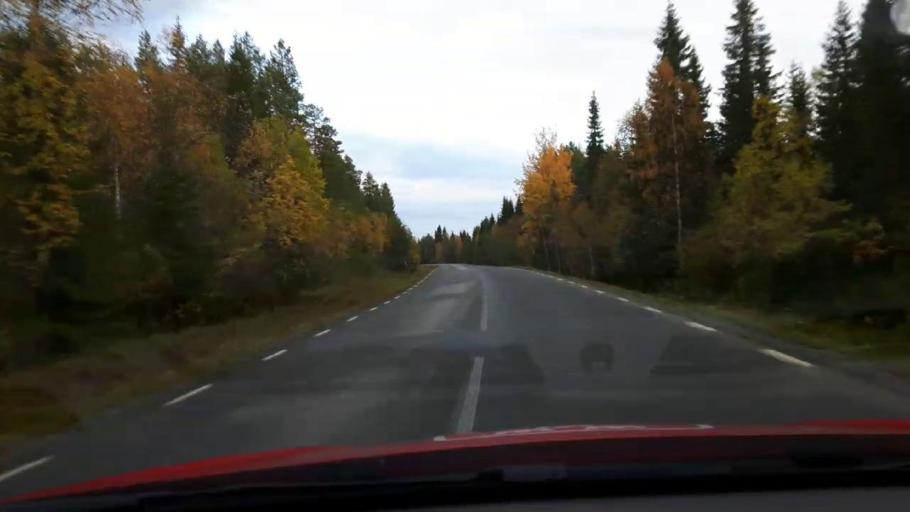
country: SE
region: Jaemtland
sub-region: OEstersunds Kommun
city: Ostersund
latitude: 63.3295
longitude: 14.6083
